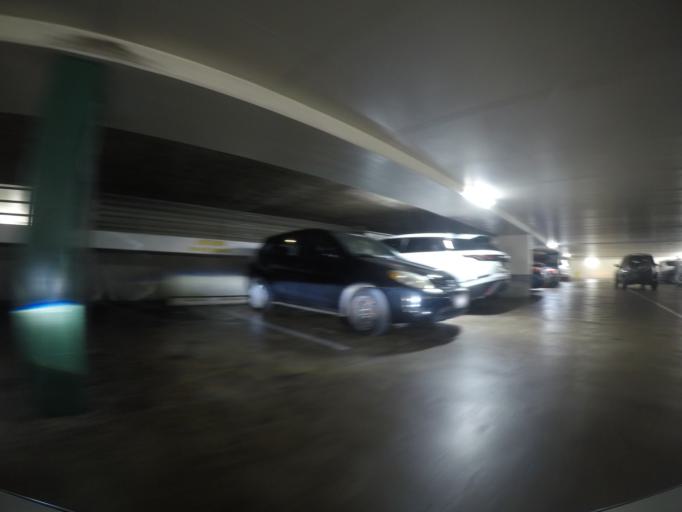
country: US
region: Hawaii
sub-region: Honolulu County
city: Honolulu
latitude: 21.2936
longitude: -157.8516
